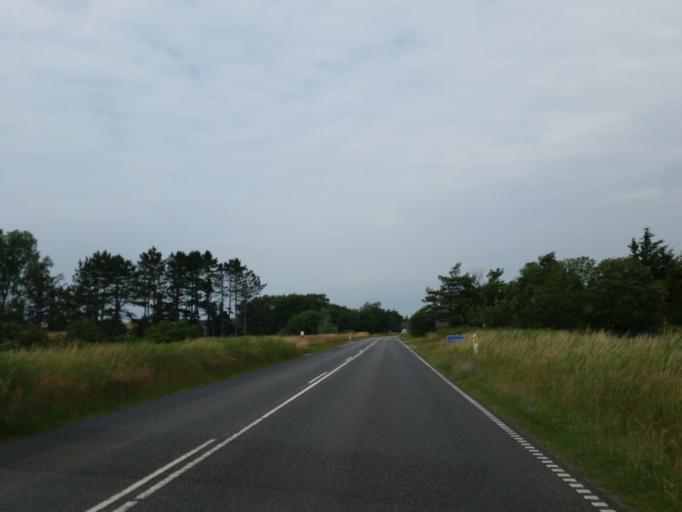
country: DE
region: Schleswig-Holstein
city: List
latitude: 55.1385
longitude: 8.5479
